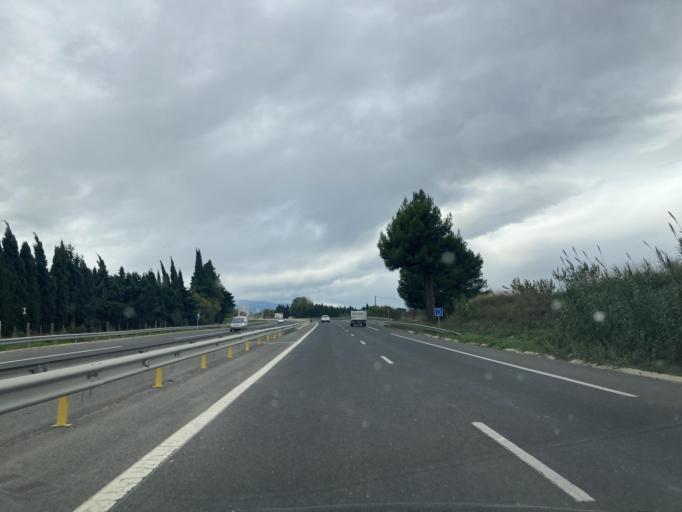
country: FR
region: Languedoc-Roussillon
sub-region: Departement des Pyrenees-Orientales
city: Elne
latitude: 42.6169
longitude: 2.9678
